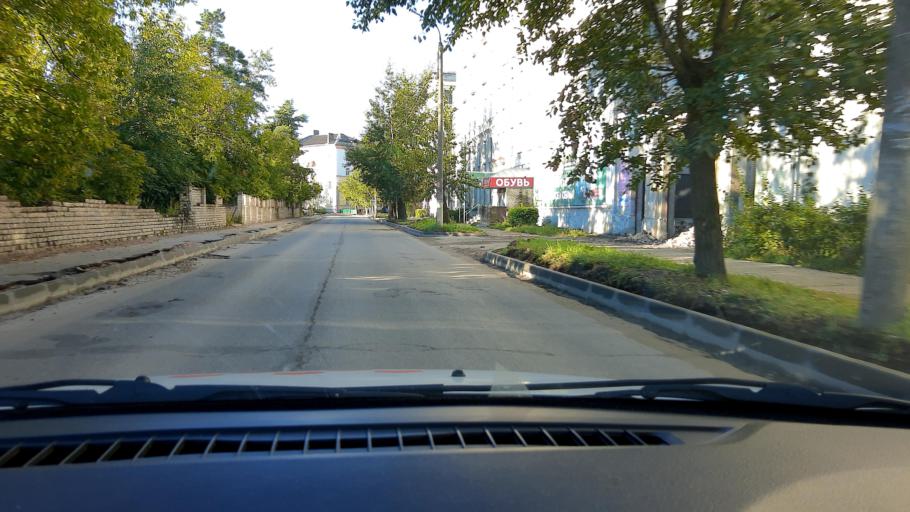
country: RU
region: Nizjnij Novgorod
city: Dzerzhinsk
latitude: 56.2451
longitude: 43.4718
